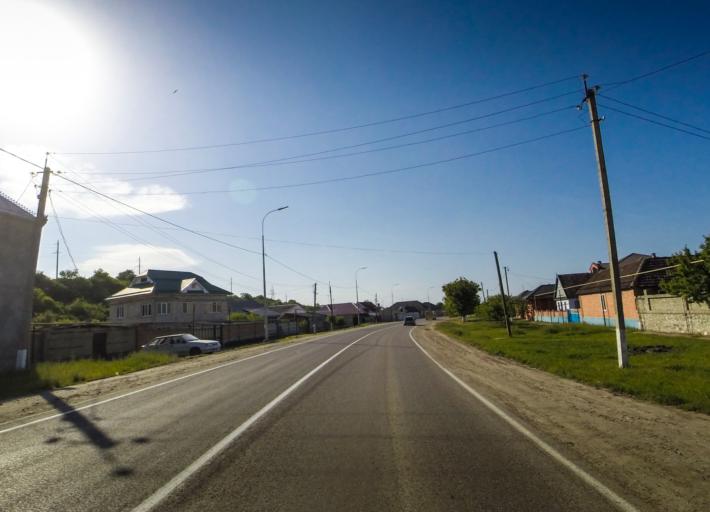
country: RU
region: Kabardino-Balkariya
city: Urvan'
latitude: 43.4750
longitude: 43.7683
